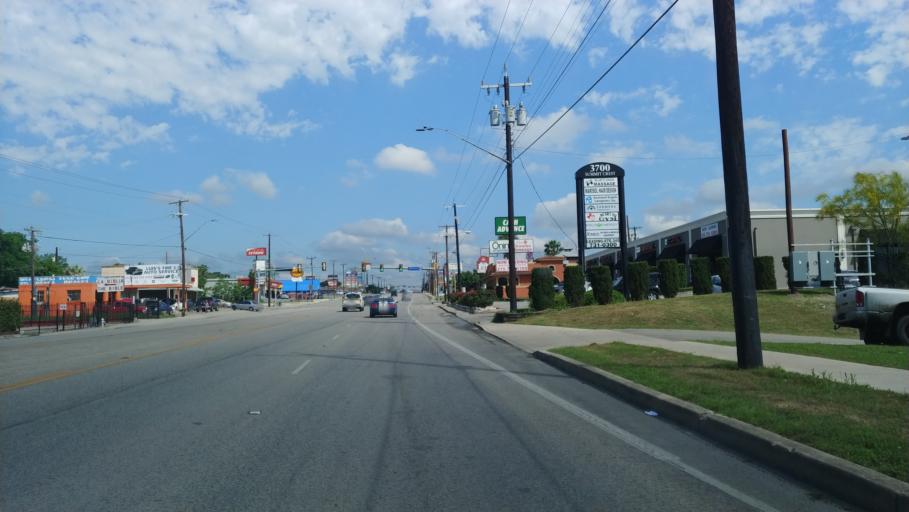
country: US
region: Texas
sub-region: Bexar County
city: Balcones Heights
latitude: 29.4806
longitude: -98.5419
